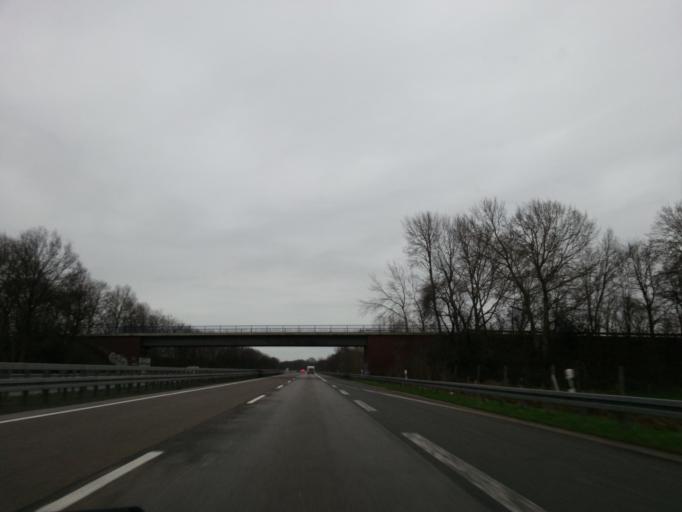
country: DE
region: North Rhine-Westphalia
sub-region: Regierungsbezirk Dusseldorf
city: Hamminkeln
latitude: 51.7610
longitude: 6.5536
